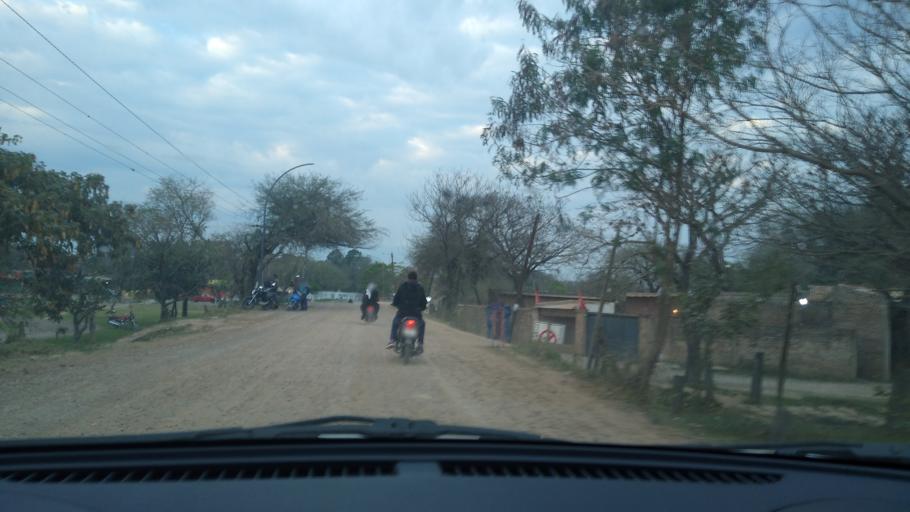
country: AR
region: Chaco
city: Barranqueras
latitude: -27.4622
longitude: -58.9516
